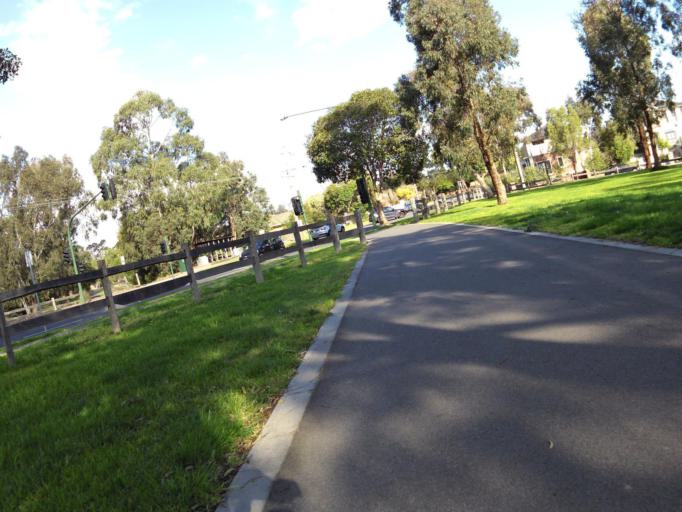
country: AU
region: Victoria
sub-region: Whitehorse
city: Box Hill North
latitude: -37.8056
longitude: 145.1259
